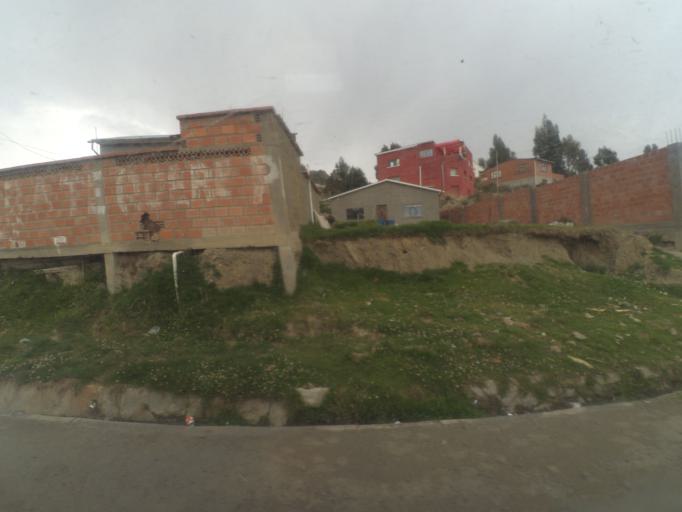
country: BO
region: La Paz
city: La Paz
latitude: -16.5693
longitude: -68.1737
